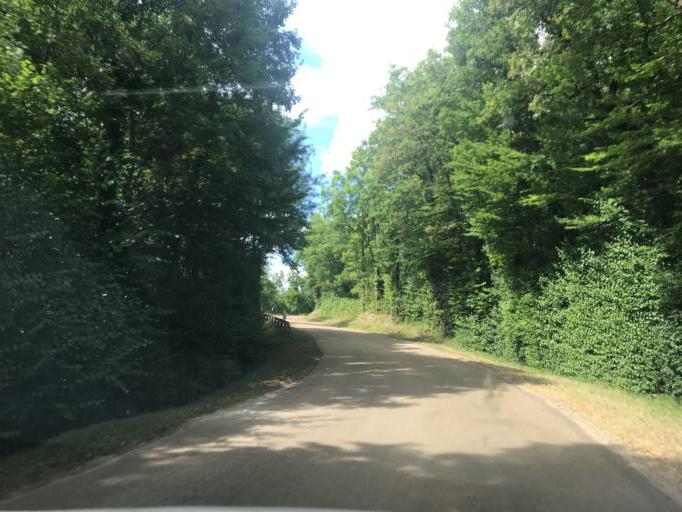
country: FR
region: Bourgogne
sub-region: Departement de l'Yonne
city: Fontenailles
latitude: 47.5602
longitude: 3.3394
